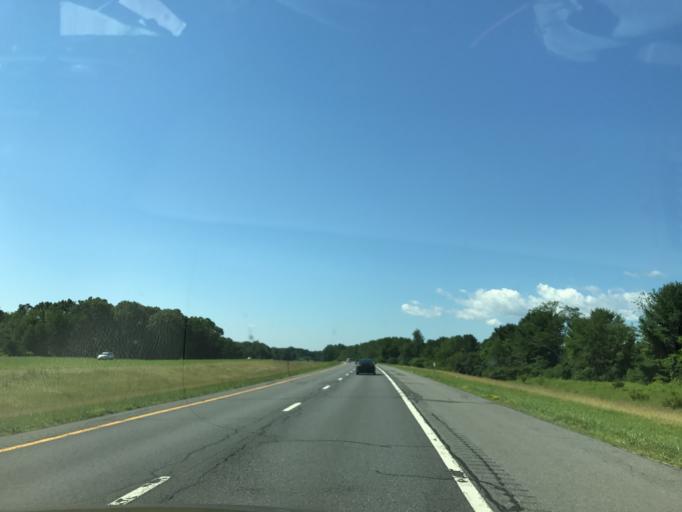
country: US
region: New York
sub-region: Rensselaer County
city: East Greenbush
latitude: 42.5382
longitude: -73.6874
